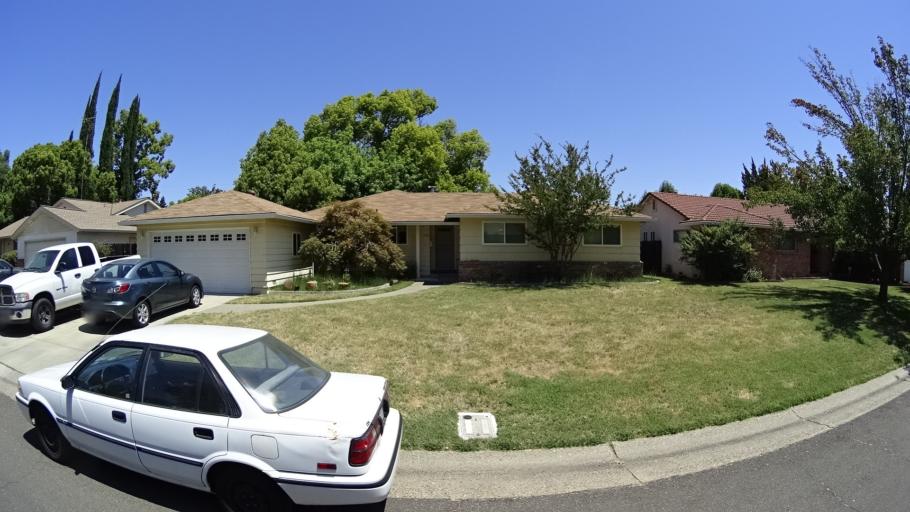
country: US
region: California
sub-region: Yolo County
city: West Sacramento
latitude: 38.5337
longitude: -121.5131
